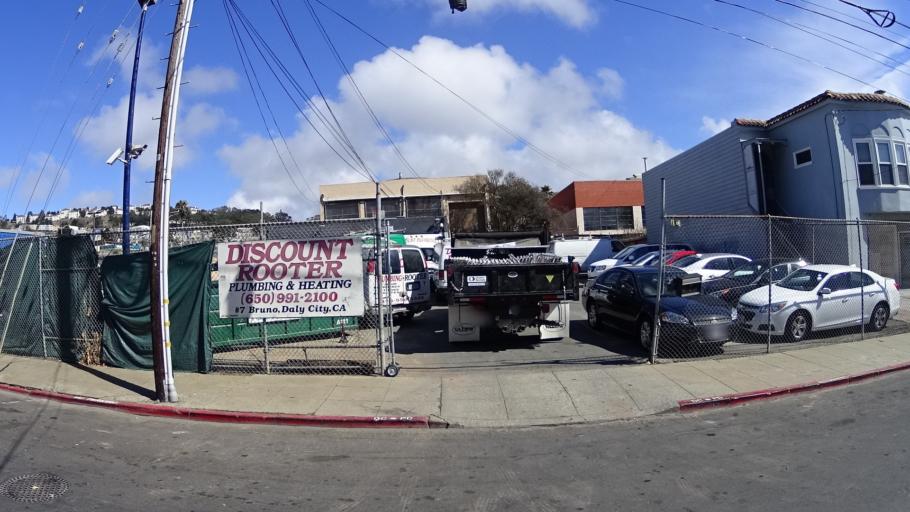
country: US
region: California
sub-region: San Mateo County
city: Daly City
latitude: 37.6951
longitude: -122.4660
